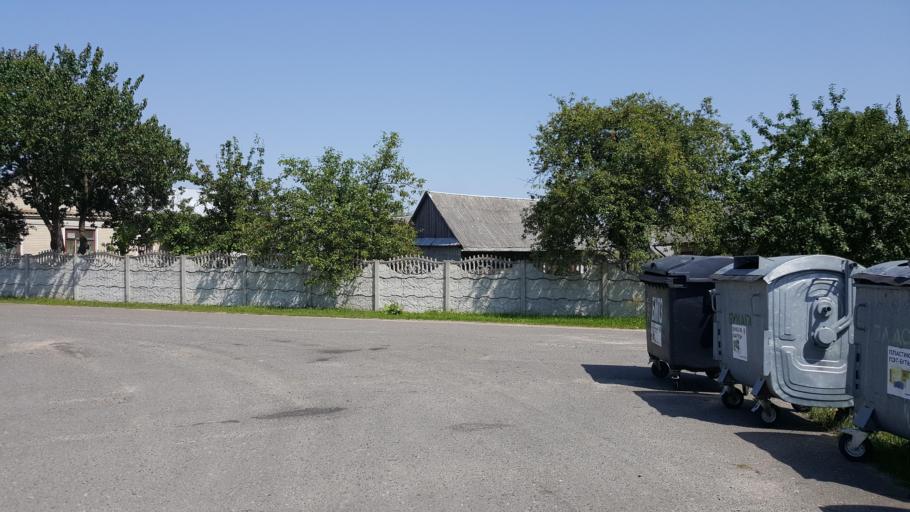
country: BY
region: Brest
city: Zhabinka
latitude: 52.1907
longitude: 24.0098
